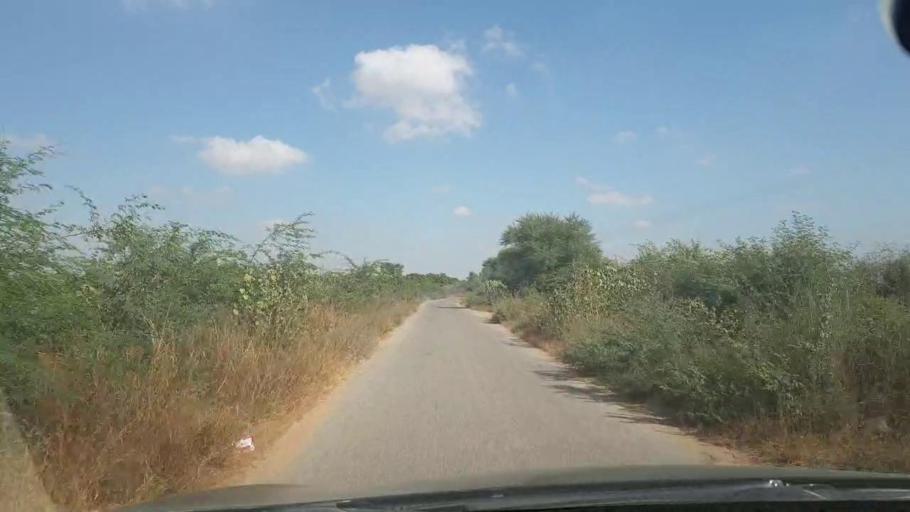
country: PK
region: Sindh
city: Malir Cantonment
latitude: 25.0549
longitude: 67.3896
